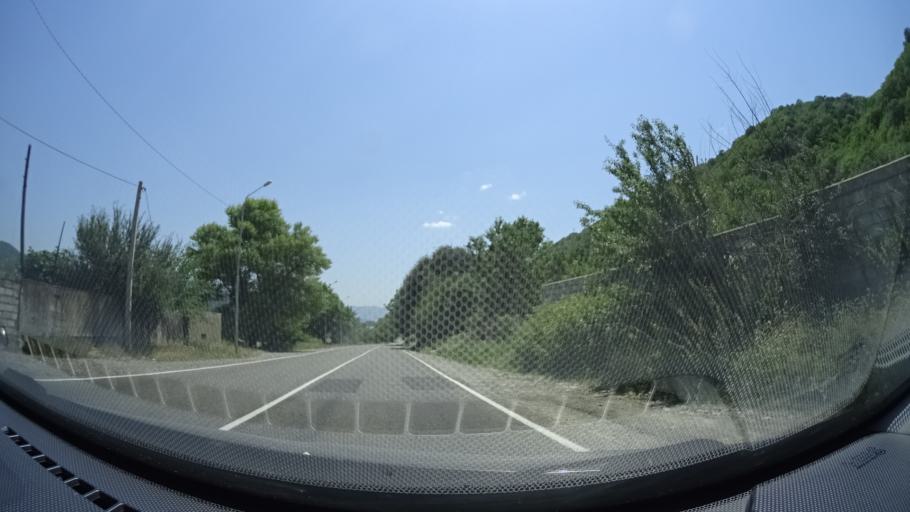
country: GE
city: Zhinvali
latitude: 42.0561
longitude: 44.7443
